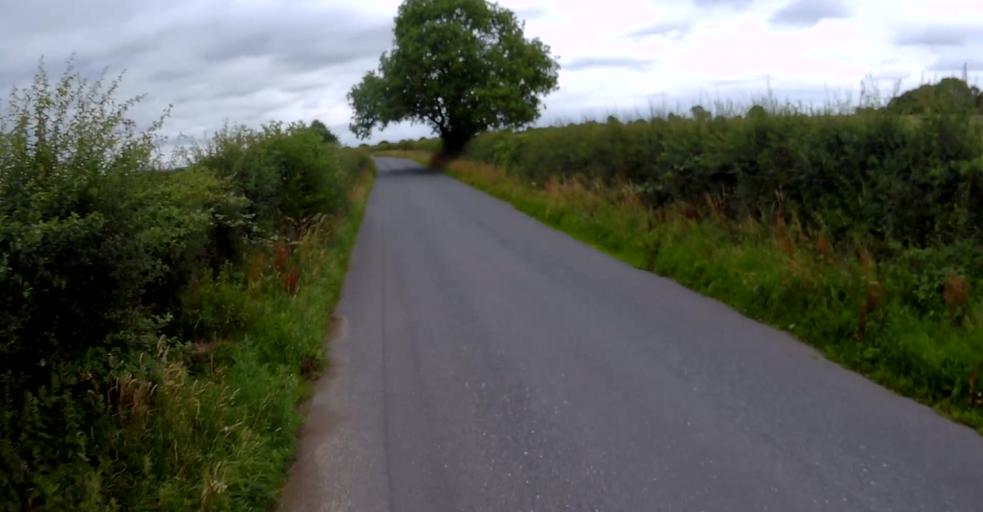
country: GB
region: England
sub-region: Hampshire
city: Four Marks
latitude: 51.1470
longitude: -1.1492
